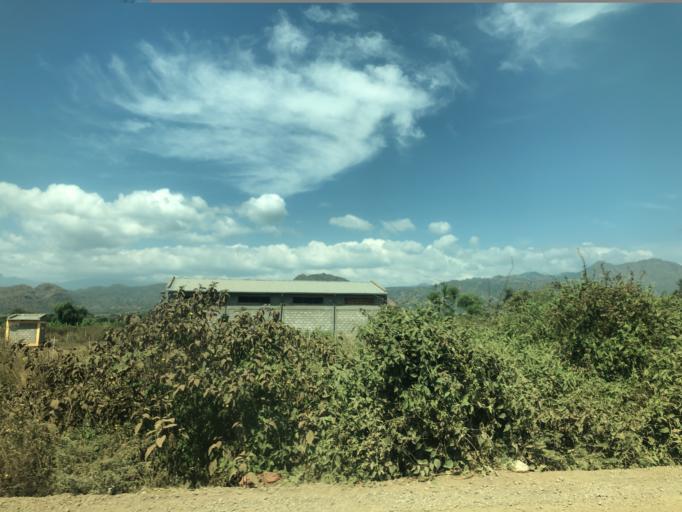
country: ET
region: Southern Nations, Nationalities, and People's Region
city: Arba Minch'
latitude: 5.9302
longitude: 37.5153
